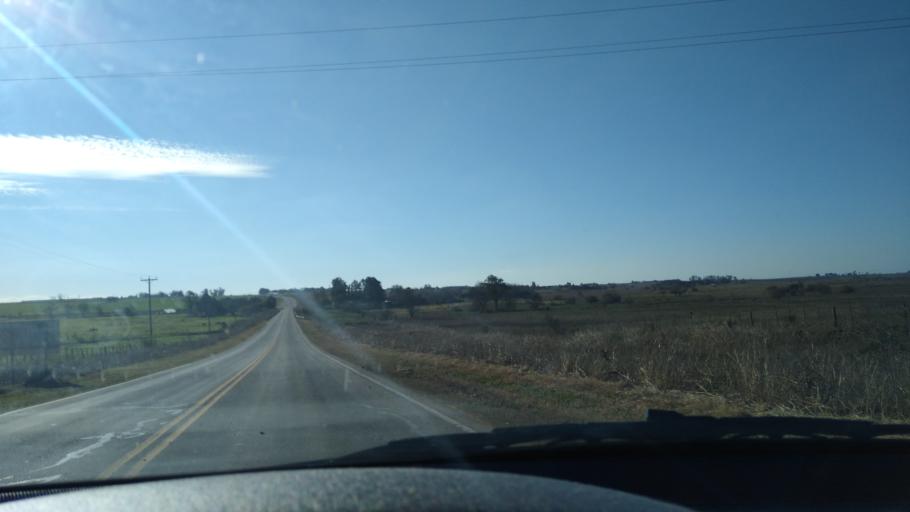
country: AR
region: Entre Rios
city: Aranguren
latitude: -32.4079
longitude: -60.3230
